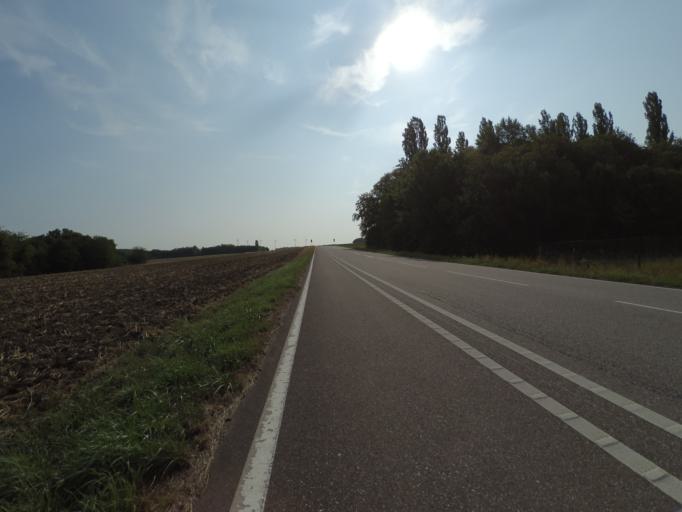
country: LU
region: Grevenmacher
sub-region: Canton de Remich
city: Remich
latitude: 49.5204
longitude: 6.3864
